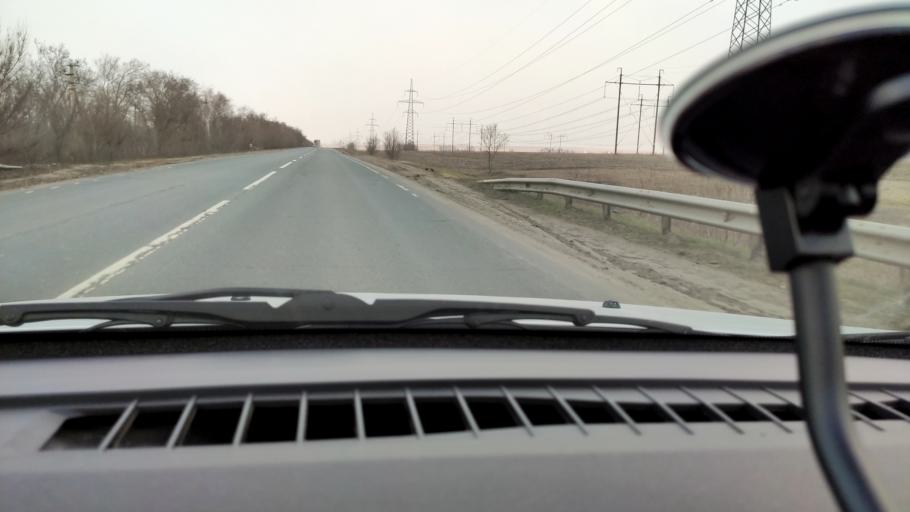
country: RU
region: Samara
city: Dubovyy Umet
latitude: 53.0735
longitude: 50.3844
